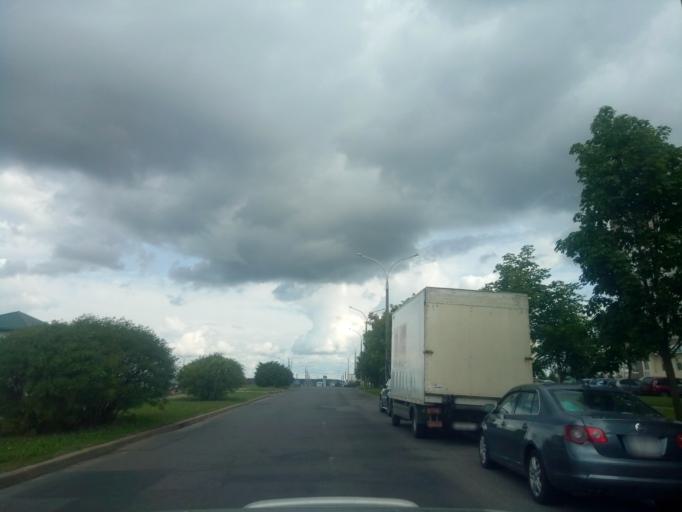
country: BY
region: Minsk
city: Novoye Medvezhino
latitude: 53.8841
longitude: 27.4176
